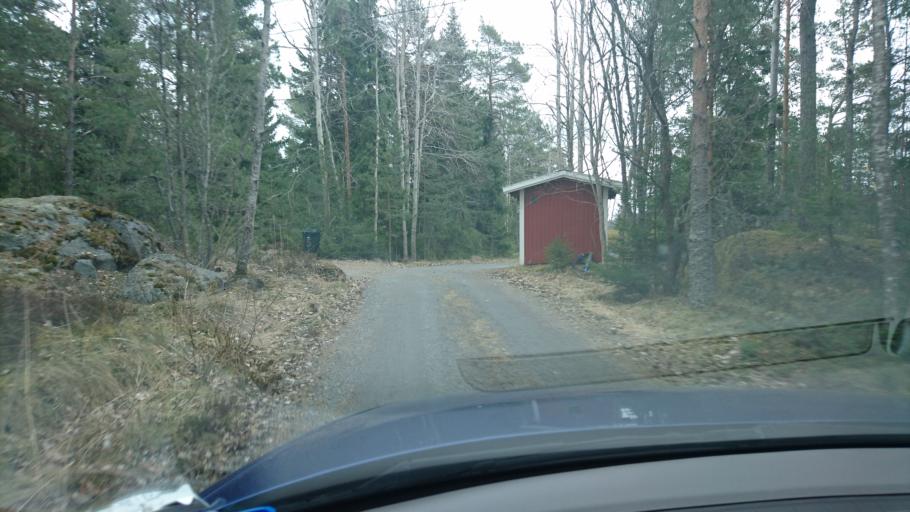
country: SE
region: Stockholm
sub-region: Norrtalje Kommun
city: Bjorko
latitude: 59.7889
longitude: 18.9877
